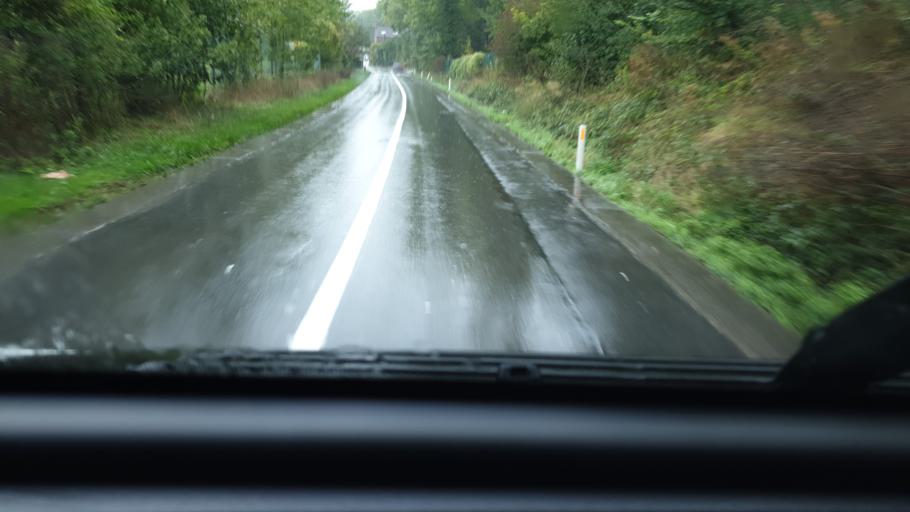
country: BE
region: Wallonia
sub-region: Province du Hainaut
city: Charleroi
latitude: 50.3702
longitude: 4.4774
